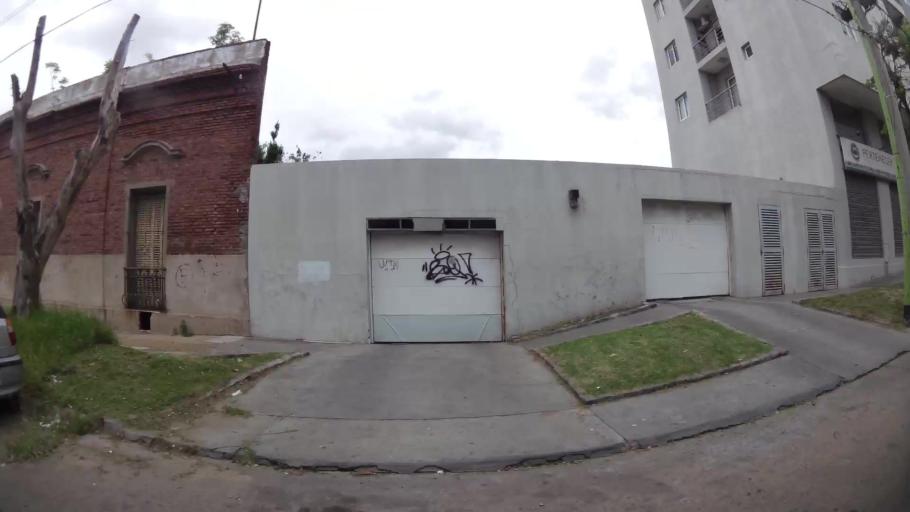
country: AR
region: Buenos Aires
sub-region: Partido de Campana
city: Campana
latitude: -34.1620
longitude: -58.9573
